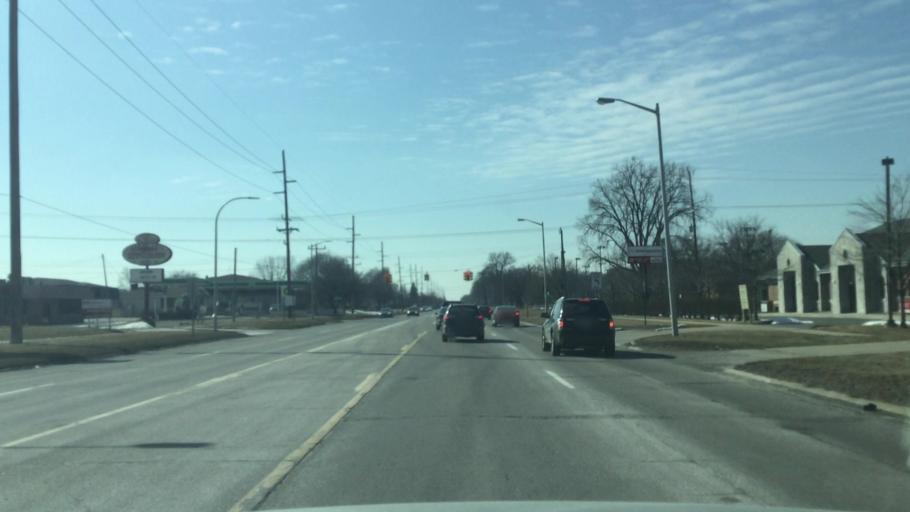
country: US
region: Michigan
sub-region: Wayne County
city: Garden City
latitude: 42.3111
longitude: -83.3387
